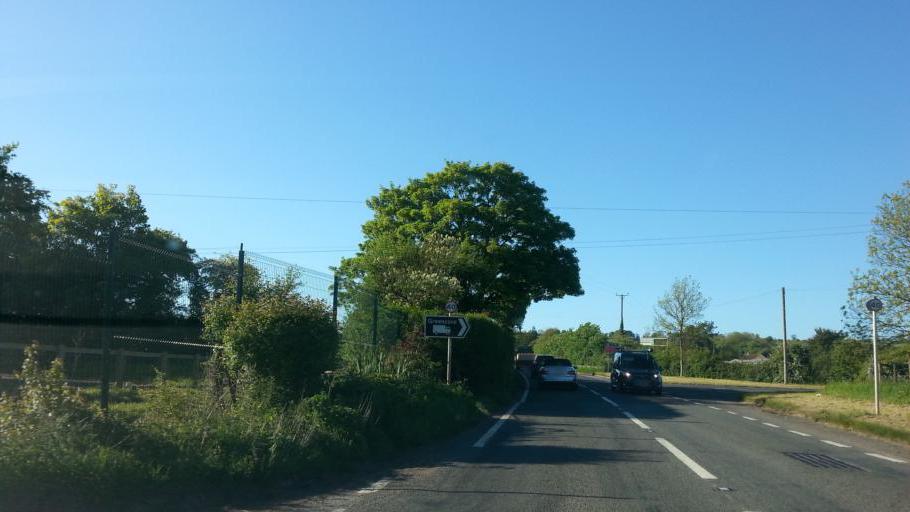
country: GB
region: England
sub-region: Somerset
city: Evercreech
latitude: 51.1578
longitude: -2.5230
